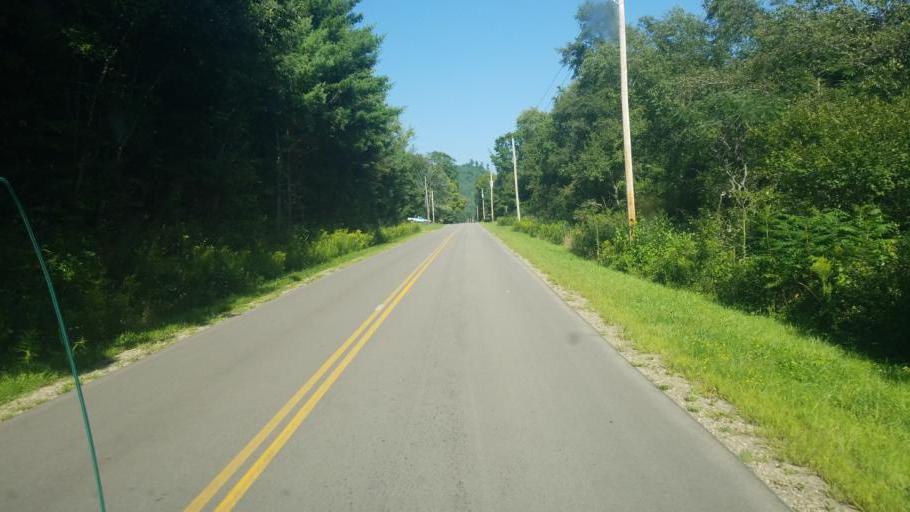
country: US
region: New York
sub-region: Allegany County
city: Wellsville
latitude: 42.0113
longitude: -78.0285
